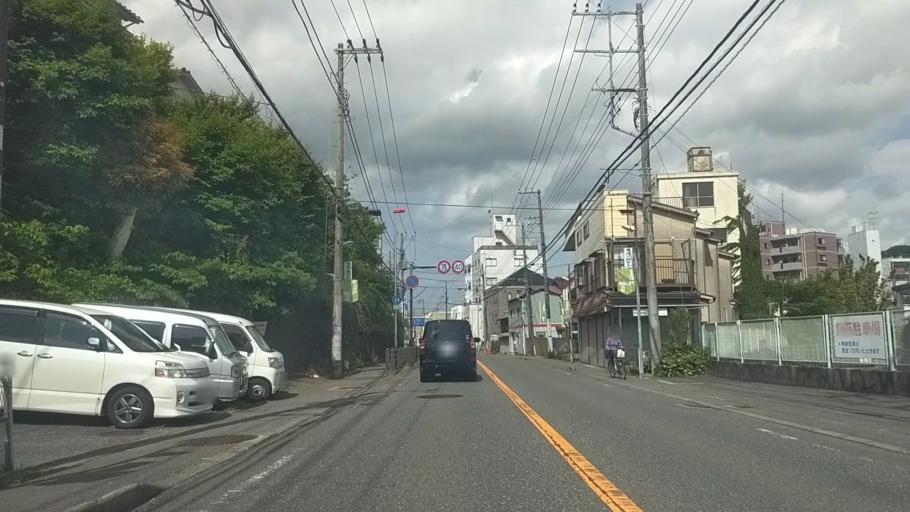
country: JP
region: Kanagawa
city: Zushi
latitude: 35.2979
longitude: 139.6025
